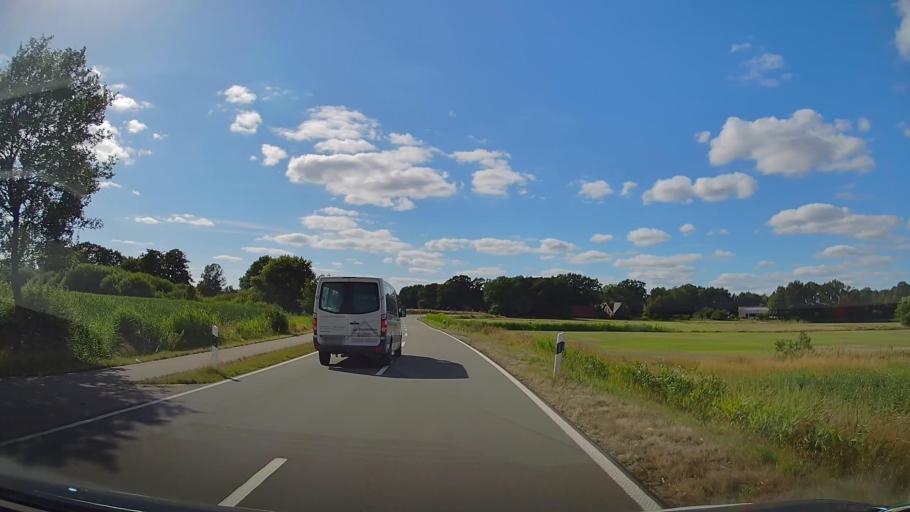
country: DE
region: Lower Saxony
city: Loningen
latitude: 52.6910
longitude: 7.7683
